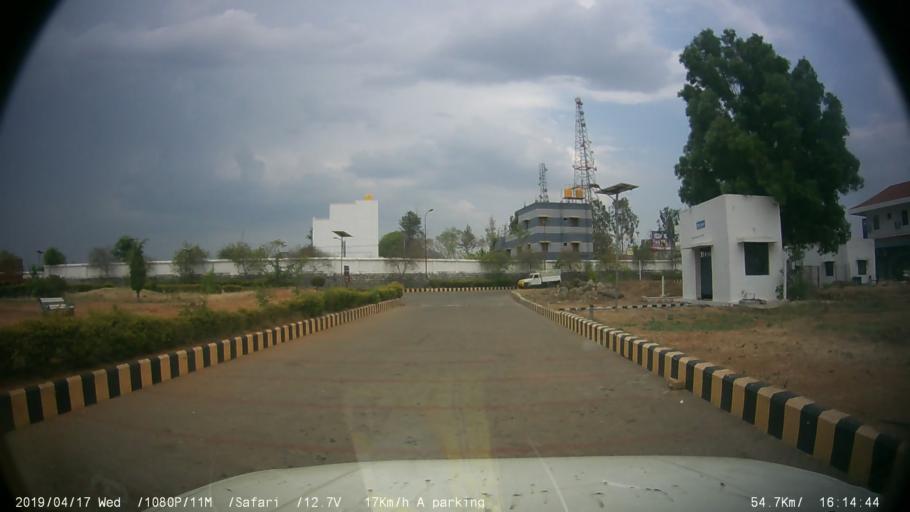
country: IN
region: Tamil Nadu
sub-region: Krishnagiri
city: Kelamangalam
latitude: 12.6669
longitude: 78.0036
